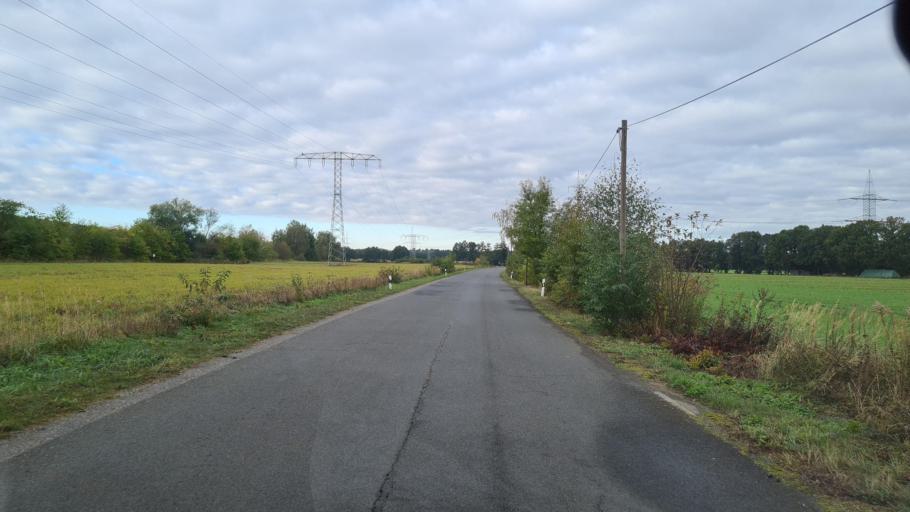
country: DE
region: Brandenburg
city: Altdobern
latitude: 51.6761
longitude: 14.0801
